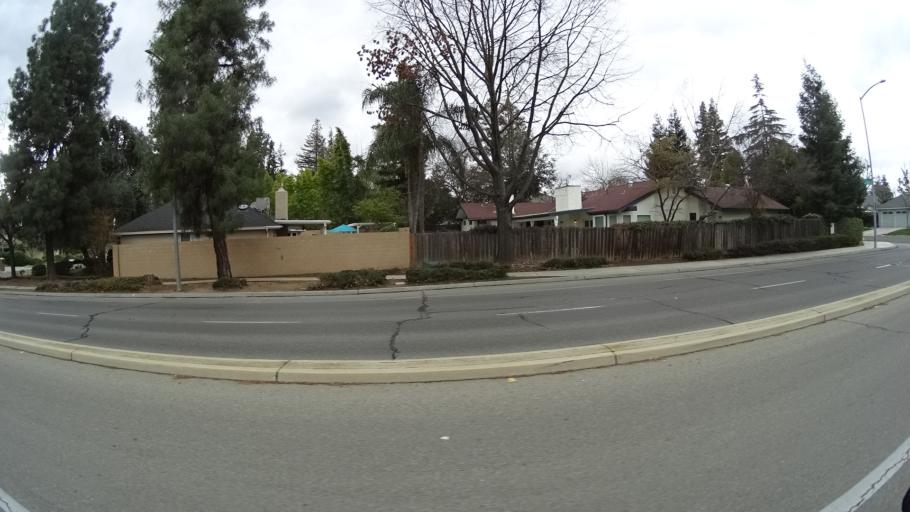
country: US
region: California
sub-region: Fresno County
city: Fresno
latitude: 36.8355
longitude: -119.8471
